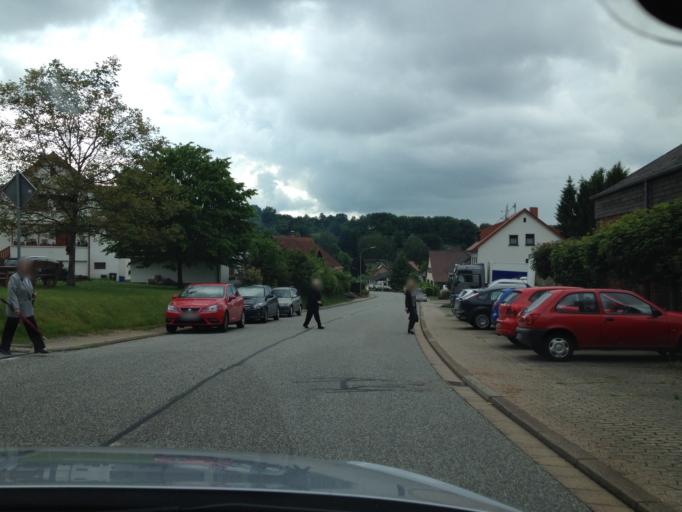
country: DE
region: Rheinland-Pfalz
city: Hahnweiler
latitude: 49.5312
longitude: 7.1908
